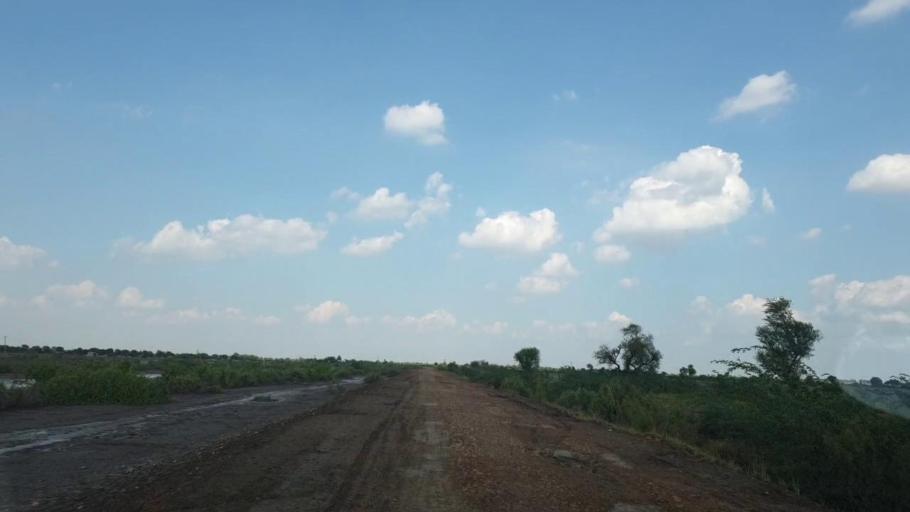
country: PK
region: Sindh
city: Pithoro
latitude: 25.6030
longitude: 69.3737
